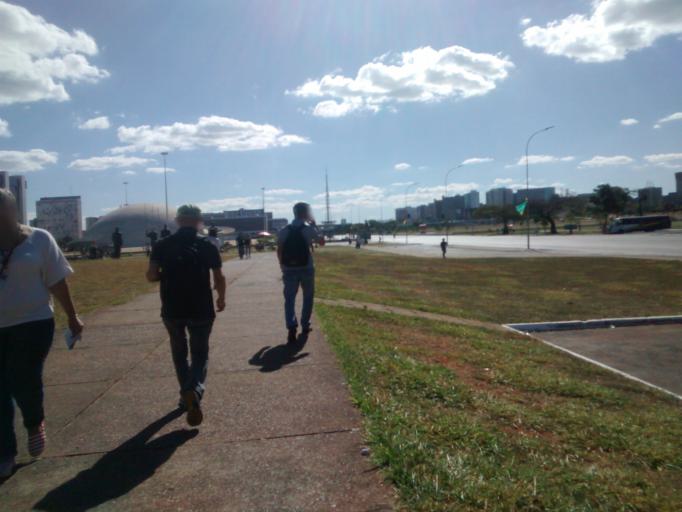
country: BR
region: Federal District
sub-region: Brasilia
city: Brasilia
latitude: -15.7978
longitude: -47.8746
